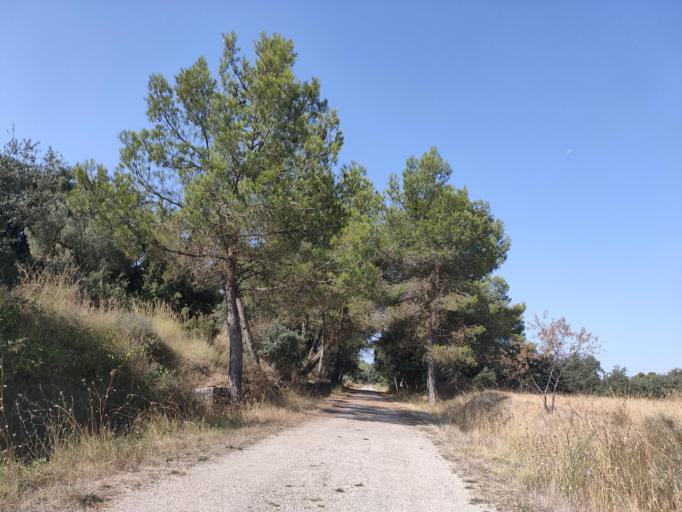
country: ES
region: Catalonia
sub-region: Provincia de Tarragona
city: Horta de Sant Joan
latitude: 40.9657
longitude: 0.3152
